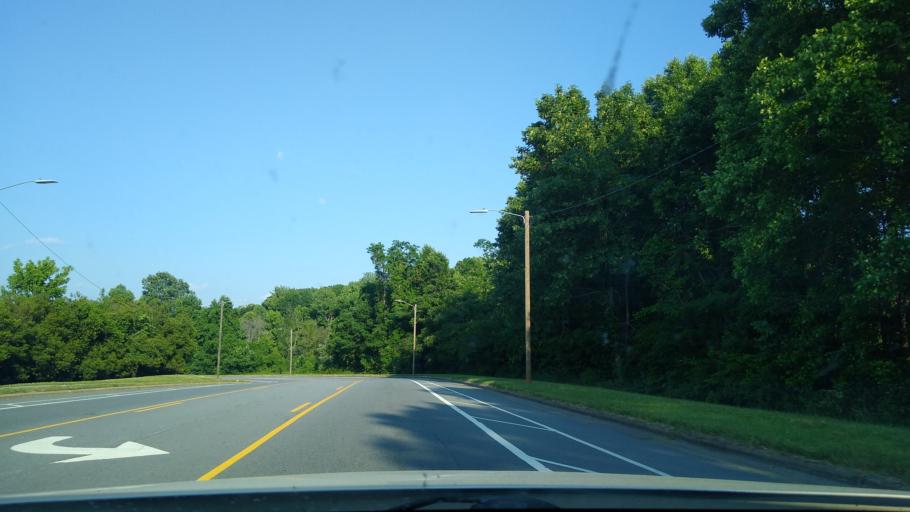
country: US
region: North Carolina
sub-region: Guilford County
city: Greensboro
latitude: 36.1069
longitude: -79.7559
